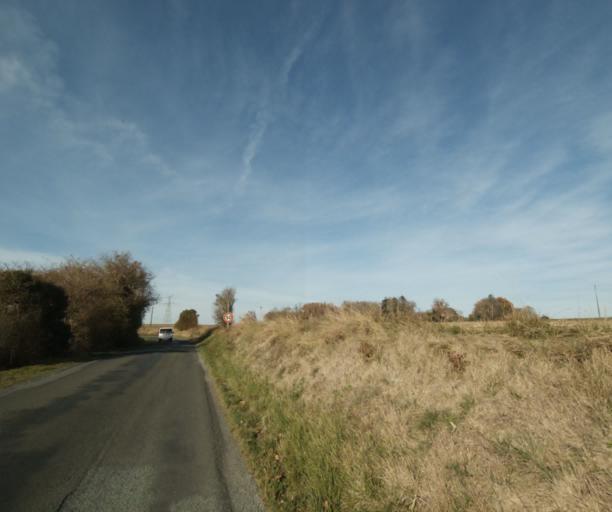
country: FR
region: Poitou-Charentes
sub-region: Departement de la Charente-Maritime
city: Les Gonds
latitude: 45.7322
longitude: -0.5892
